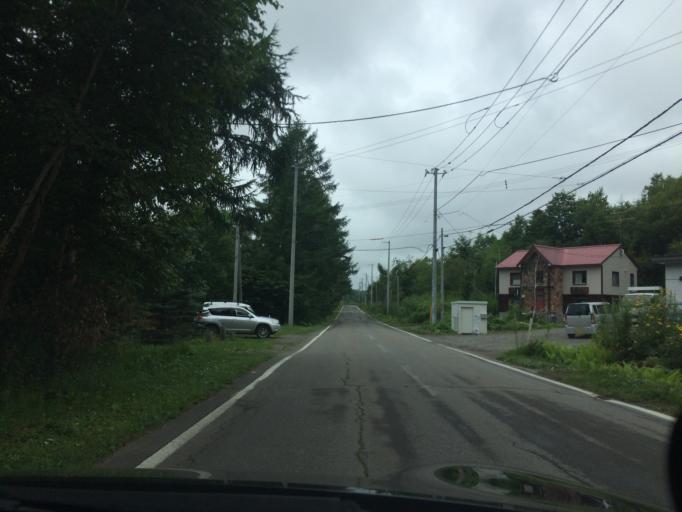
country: JP
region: Hokkaido
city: Otofuke
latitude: 42.9617
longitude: 143.1224
